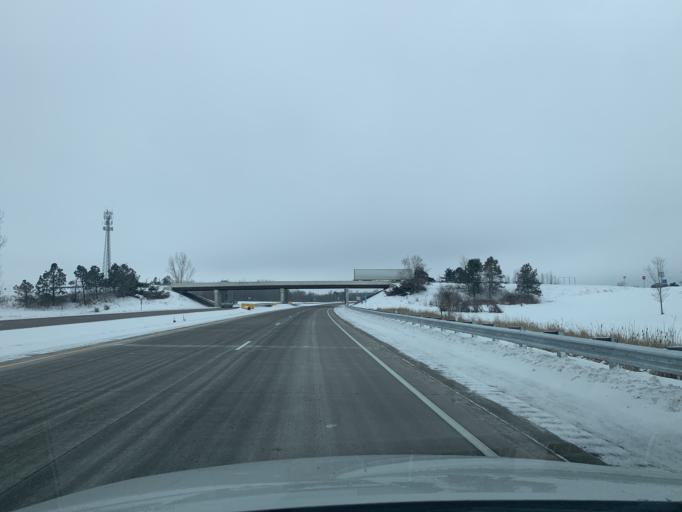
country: US
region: Minnesota
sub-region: Chisago County
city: Rush City
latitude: 45.6857
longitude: -92.9900
